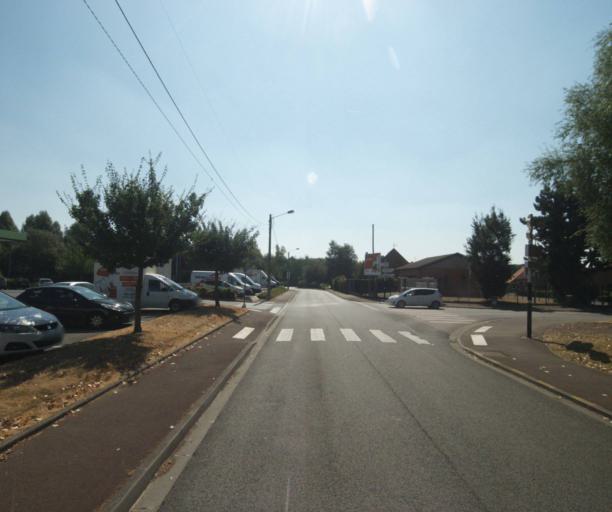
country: FR
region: Nord-Pas-de-Calais
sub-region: Departement du Nord
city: Bousbecque
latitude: 50.7700
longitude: 3.0833
